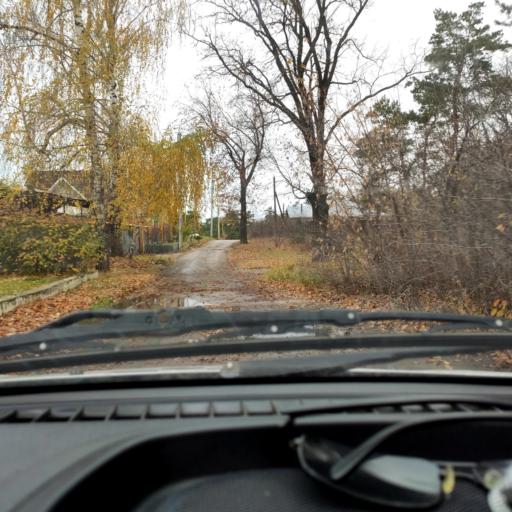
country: RU
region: Samara
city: Tol'yatti
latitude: 53.4809
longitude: 49.3573
